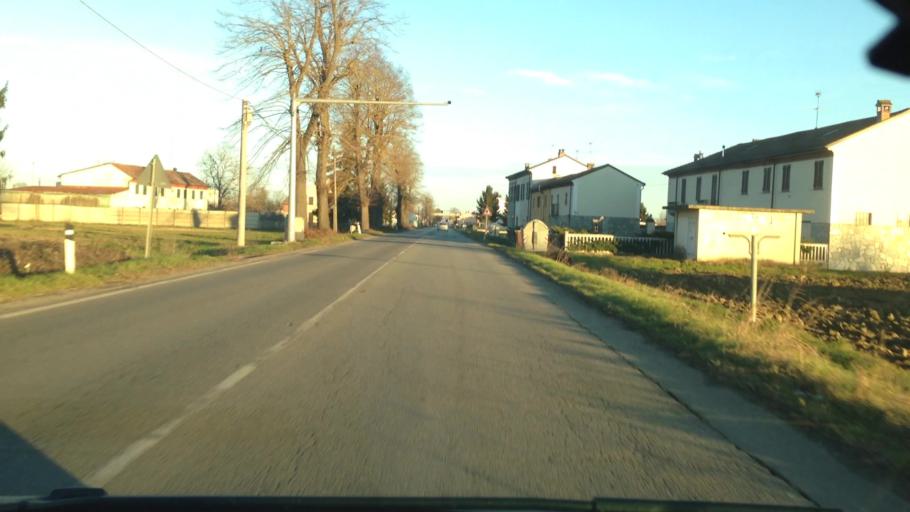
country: IT
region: Piedmont
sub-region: Provincia di Alessandria
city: Alessandria
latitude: 44.9216
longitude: 8.5650
